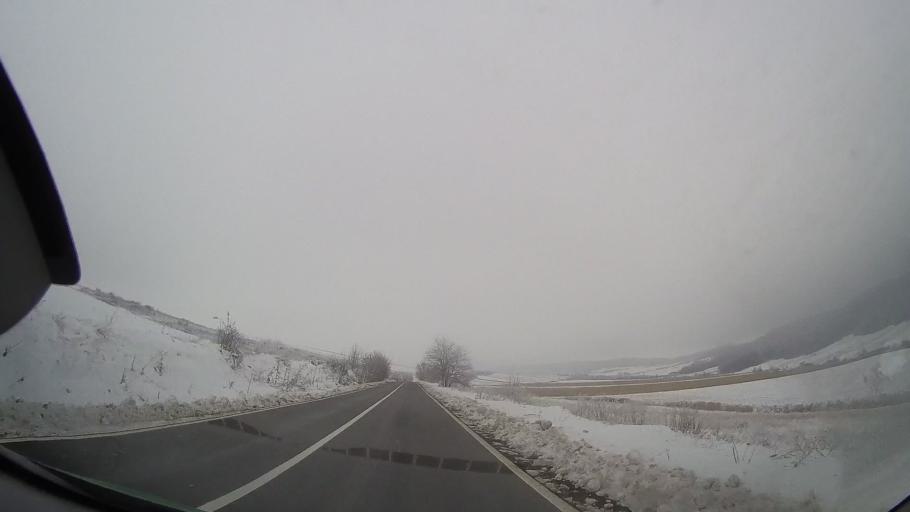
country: RO
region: Neamt
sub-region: Comuna Poenari
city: Poienari
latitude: 46.8717
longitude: 27.1429
